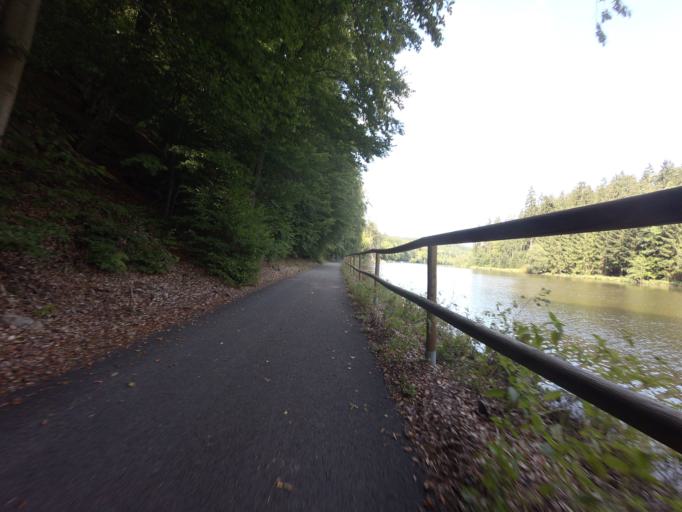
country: CZ
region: Jihocesky
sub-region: Okres Ceske Budejovice
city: Hluboka nad Vltavou
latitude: 49.0752
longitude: 14.4549
